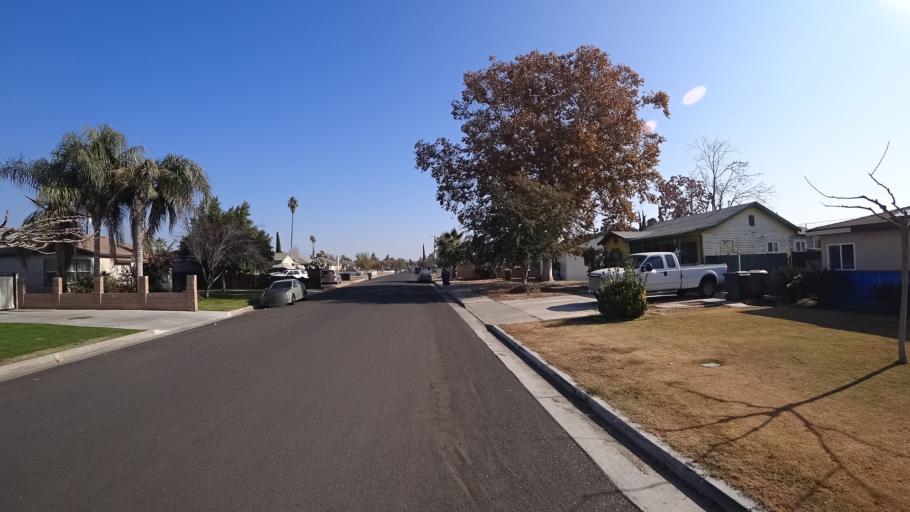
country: US
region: California
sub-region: Kern County
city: Bakersfield
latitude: 35.3449
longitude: -119.0253
